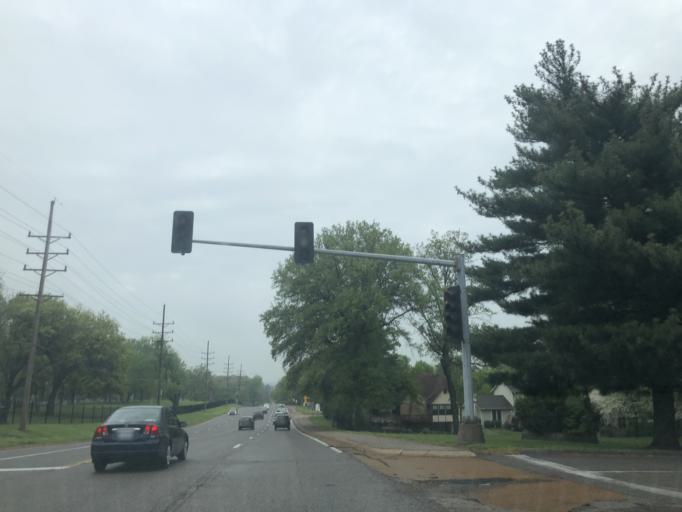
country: US
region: Missouri
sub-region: Saint Louis County
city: Marlborough
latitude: 38.5732
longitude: -90.3197
